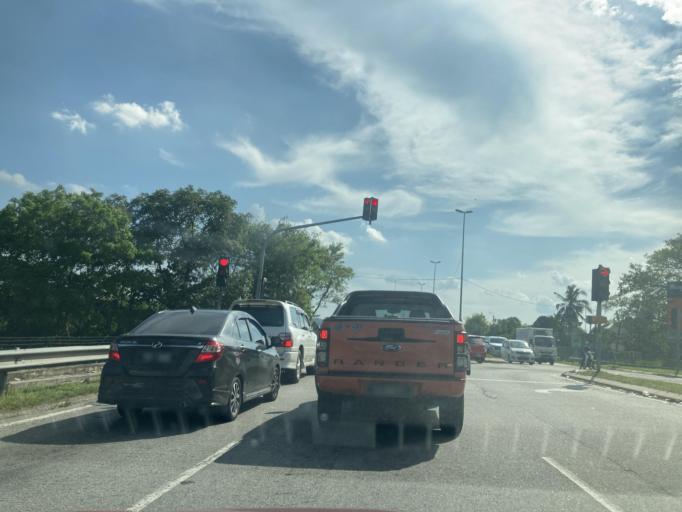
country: MY
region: Selangor
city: Kampung Baru Subang
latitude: 3.1501
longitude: 101.5416
